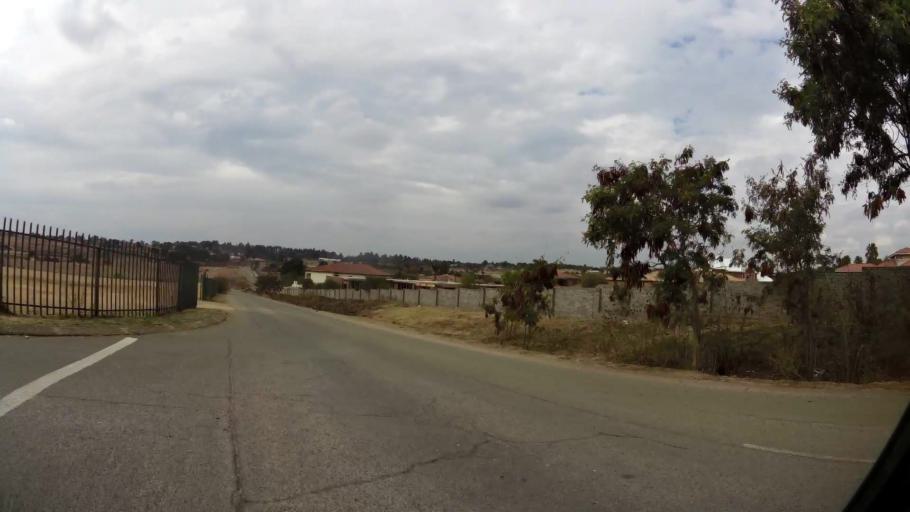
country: ZA
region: Gauteng
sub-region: West Rand District Municipality
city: Muldersdriseloop
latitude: -26.0752
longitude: 27.8656
